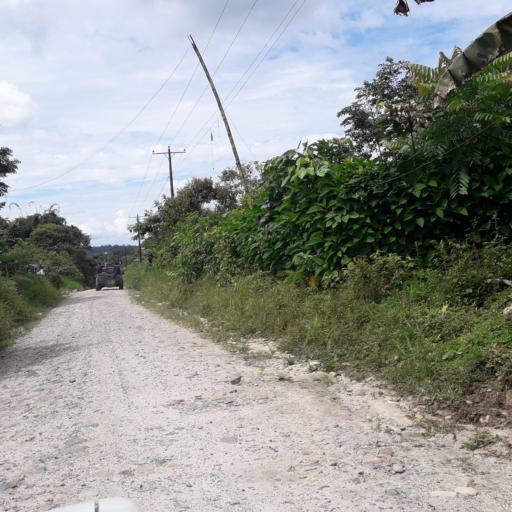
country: EC
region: Napo
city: Archidona
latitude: -0.9415
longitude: -77.8753
